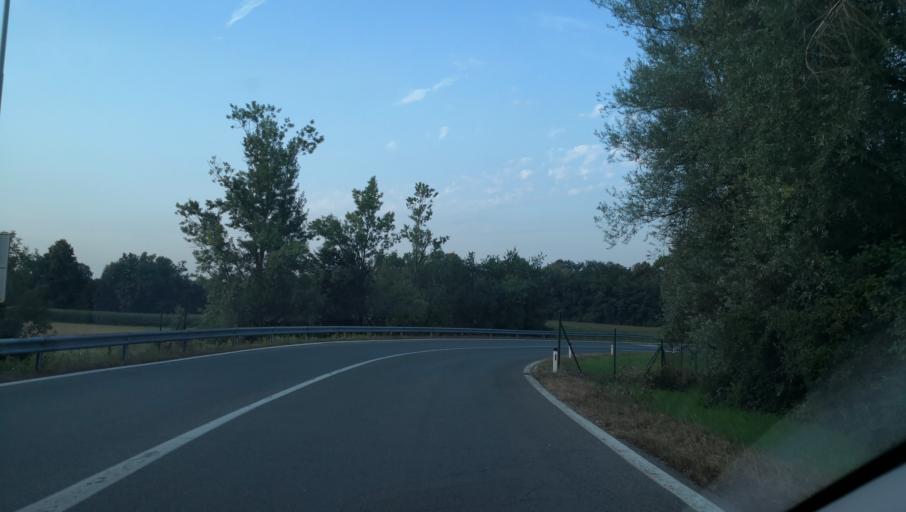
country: SI
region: Medvode
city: Zgornje Pirnice
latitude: 46.1233
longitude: 14.4832
